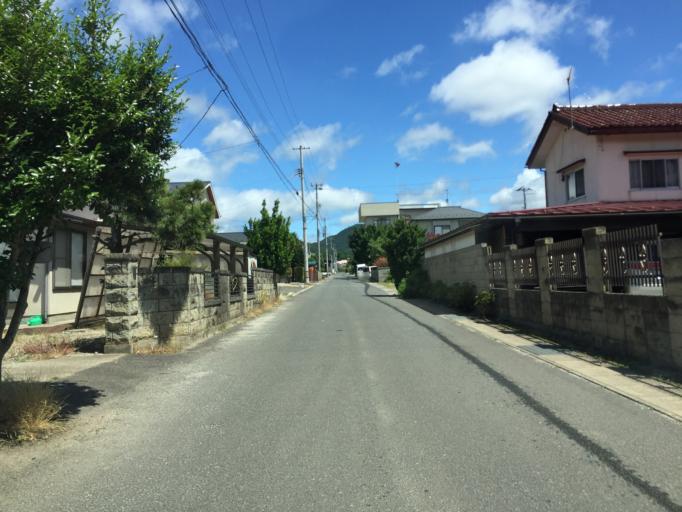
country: JP
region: Fukushima
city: Fukushima-shi
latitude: 37.8139
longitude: 140.4247
